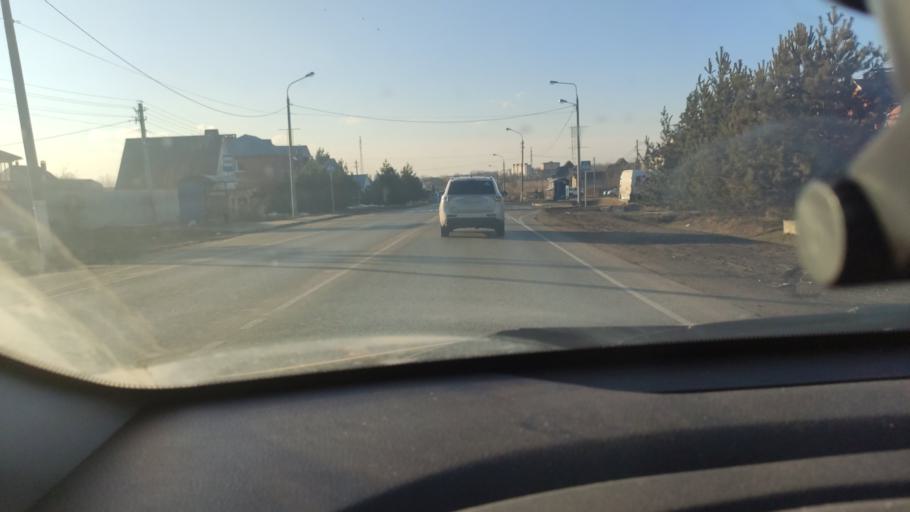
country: RU
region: Moskovskaya
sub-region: Chekhovskiy Rayon
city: Chekhov
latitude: 55.1547
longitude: 37.4497
